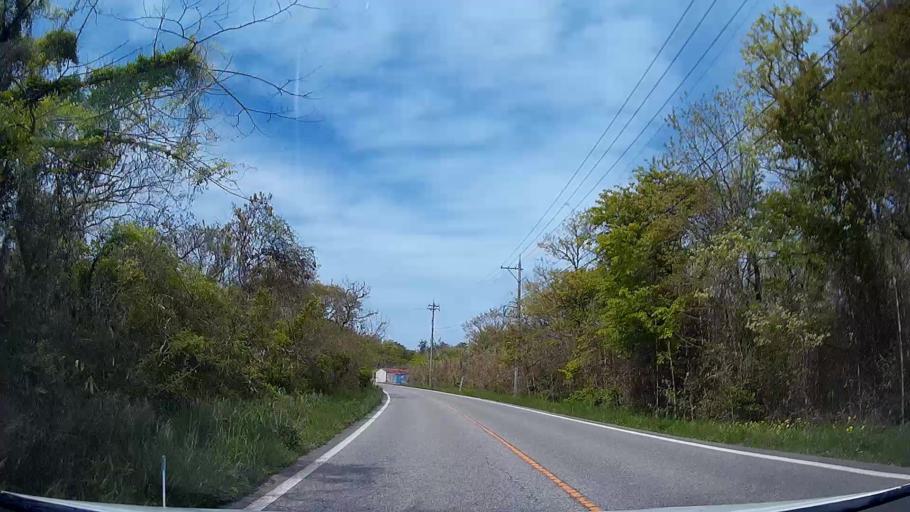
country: JP
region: Ishikawa
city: Hakui
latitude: 36.9612
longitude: 136.7733
